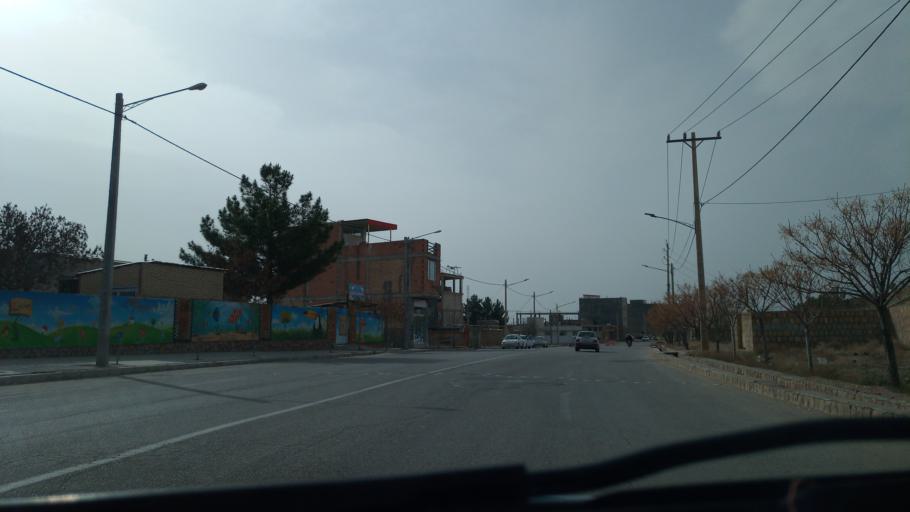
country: IR
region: Khorasan-e Shomali
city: Esfarayen
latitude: 37.0852
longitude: 57.5014
